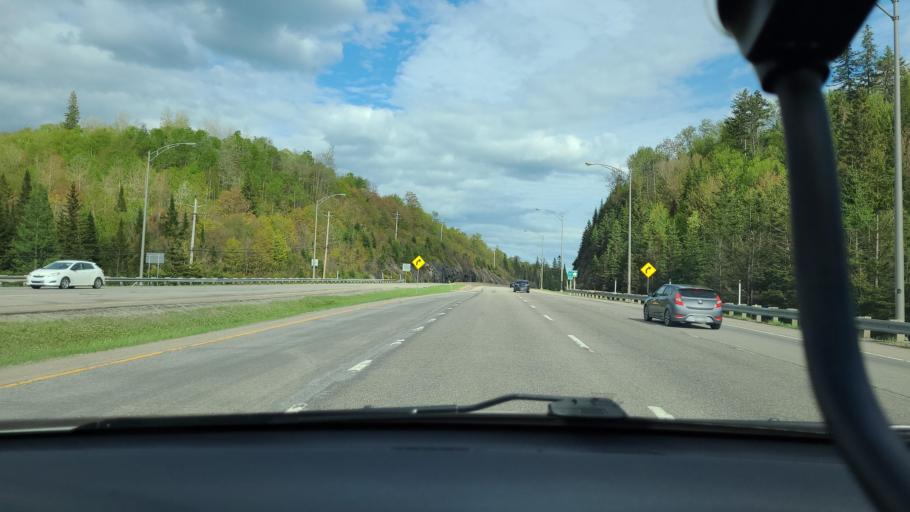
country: CA
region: Quebec
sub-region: Laurentides
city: Sainte-Agathe-des-Monts
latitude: 46.0893
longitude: -74.3300
